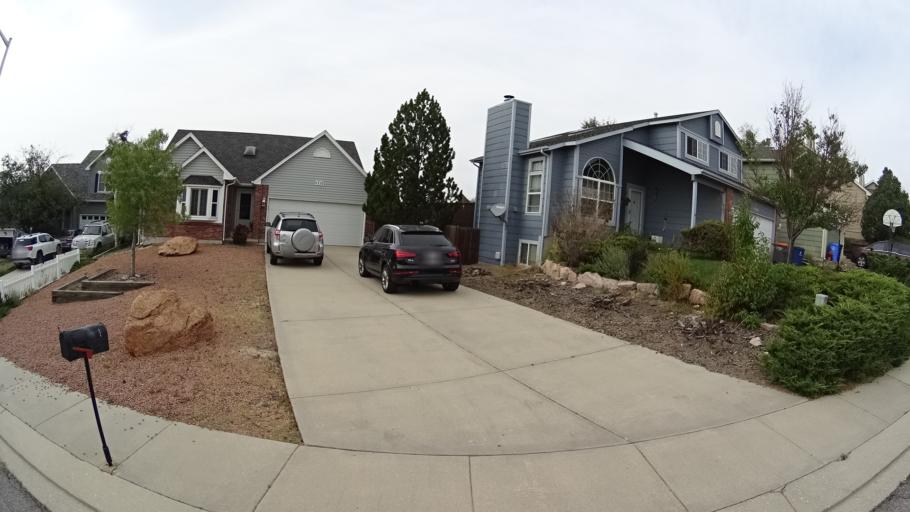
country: US
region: Colorado
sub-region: El Paso County
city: Cimarron Hills
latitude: 38.9090
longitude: -104.7288
